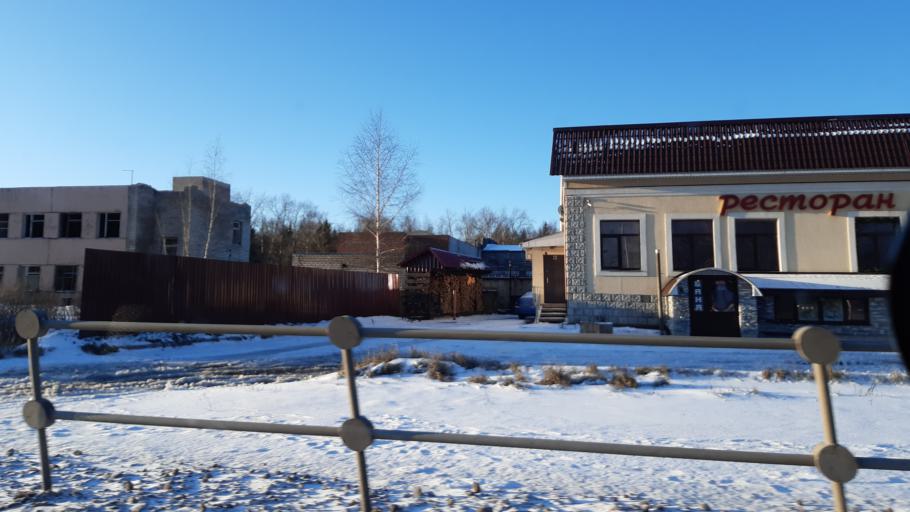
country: RU
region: Moskovskaya
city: Skoropuskovskiy
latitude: 56.3398
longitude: 38.1644
